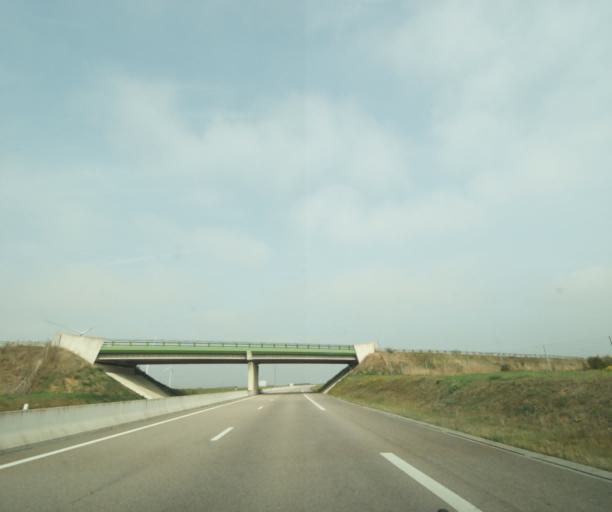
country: FR
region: Lower Normandy
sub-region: Departement de l'Orne
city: Argentan
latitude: 48.7096
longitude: -0.0521
